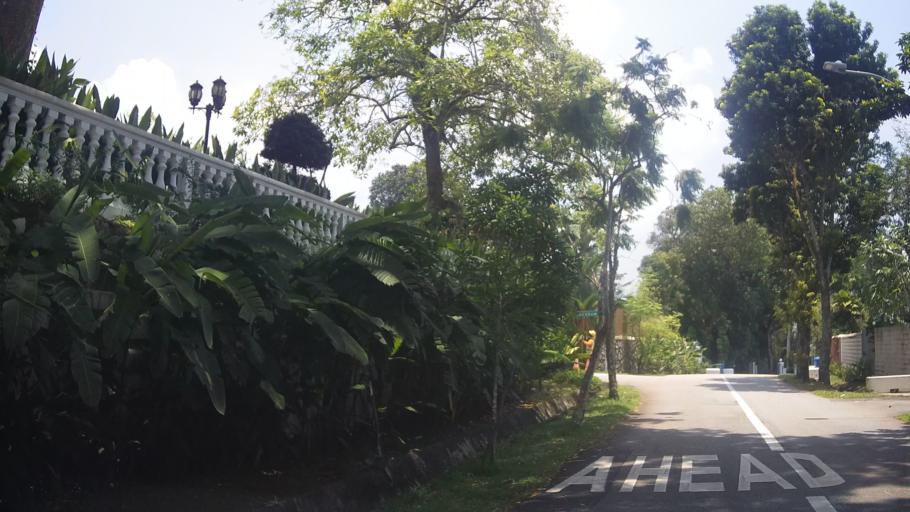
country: SG
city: Singapore
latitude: 1.3383
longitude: 103.7837
